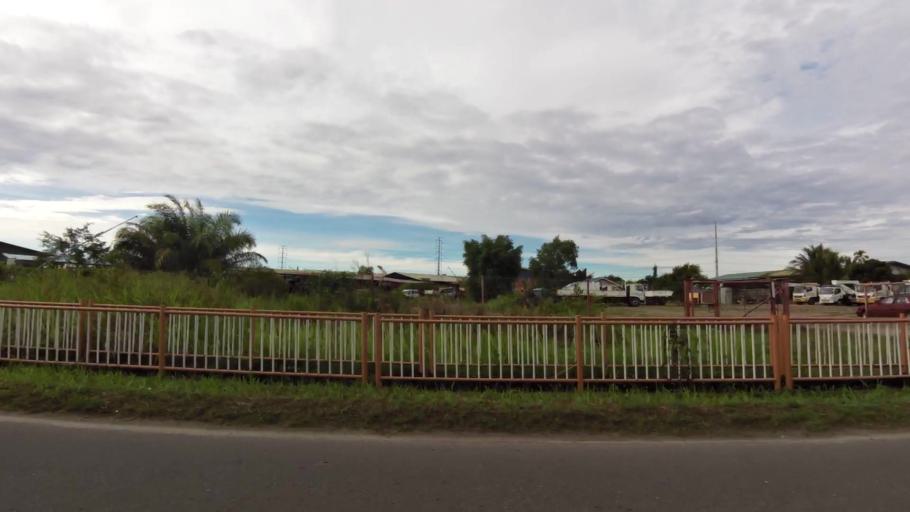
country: BN
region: Belait
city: Seria
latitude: 4.6142
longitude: 114.3537
